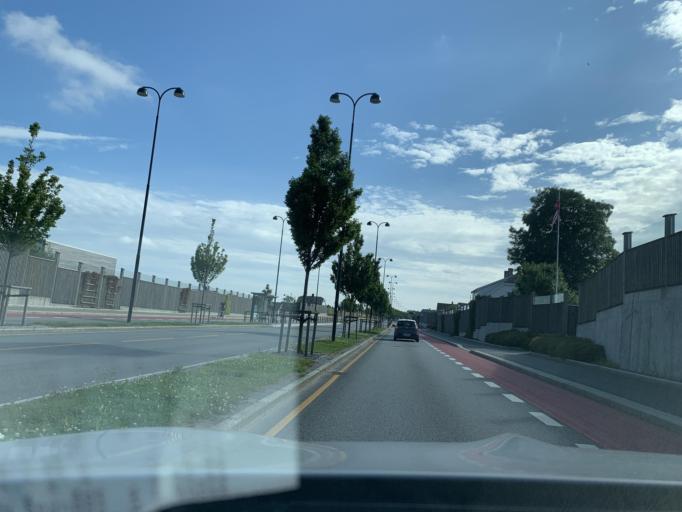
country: NO
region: Rogaland
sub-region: Stavanger
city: Stavanger
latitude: 58.9321
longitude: 5.7387
